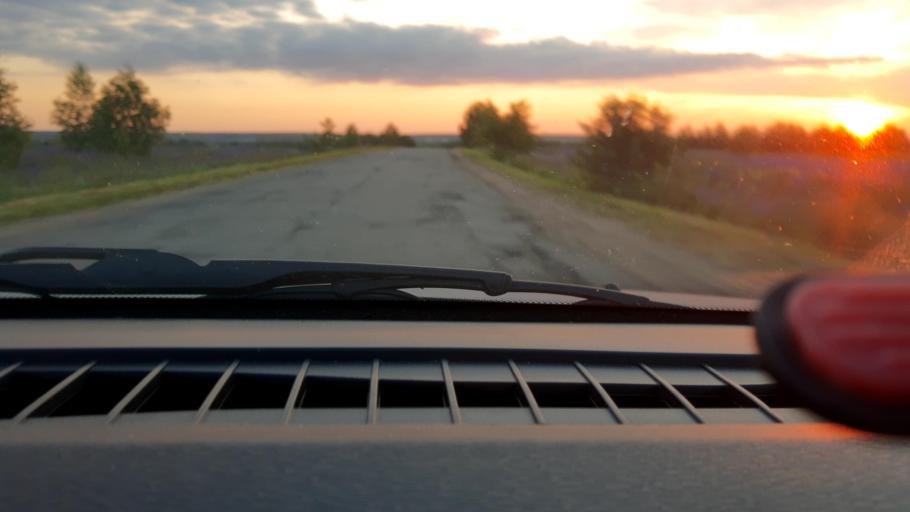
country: RU
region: Nizjnij Novgorod
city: Surovatikha
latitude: 55.8492
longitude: 43.9509
